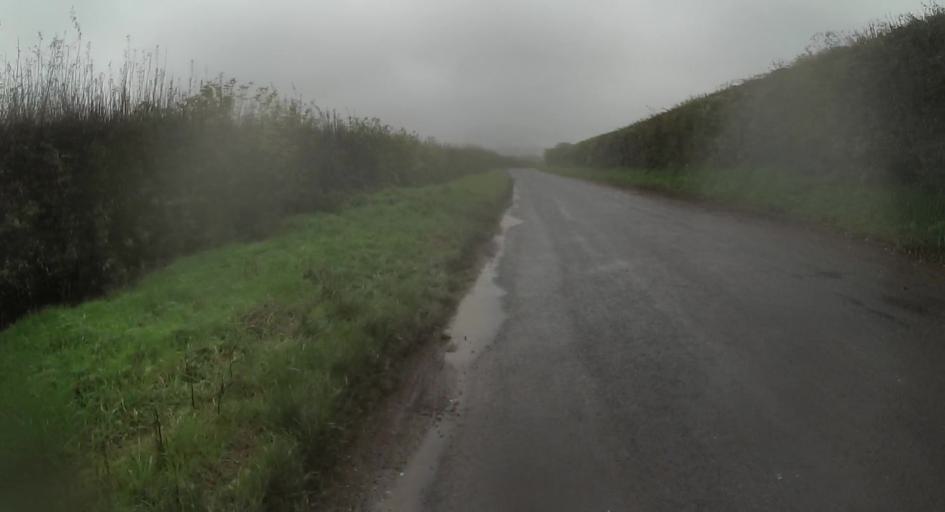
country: GB
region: England
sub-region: Hampshire
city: Four Marks
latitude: 51.1627
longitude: -1.1263
